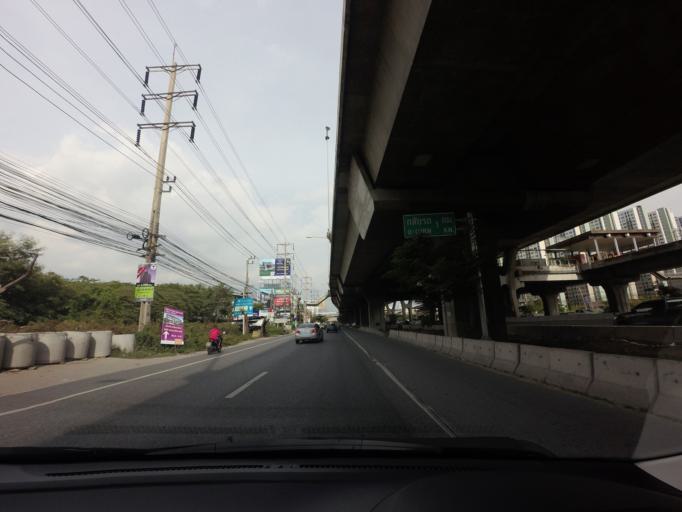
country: TH
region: Bangkok
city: Bang Na
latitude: 13.6567
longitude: 100.6705
